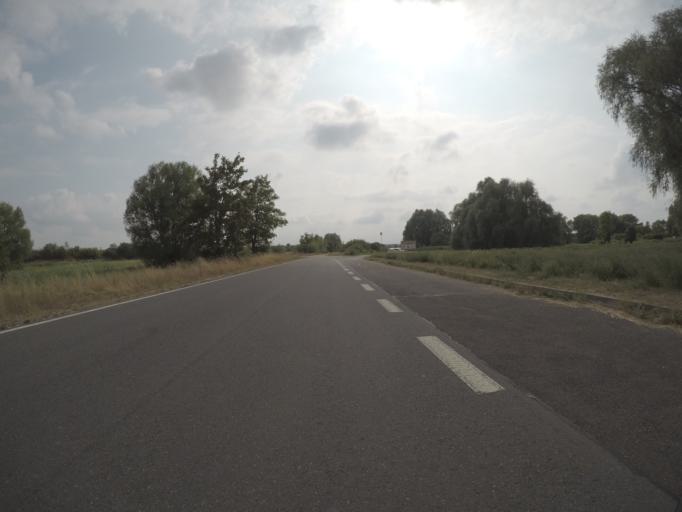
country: DE
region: Brandenburg
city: Schonefeld
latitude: 52.3704
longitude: 13.4746
